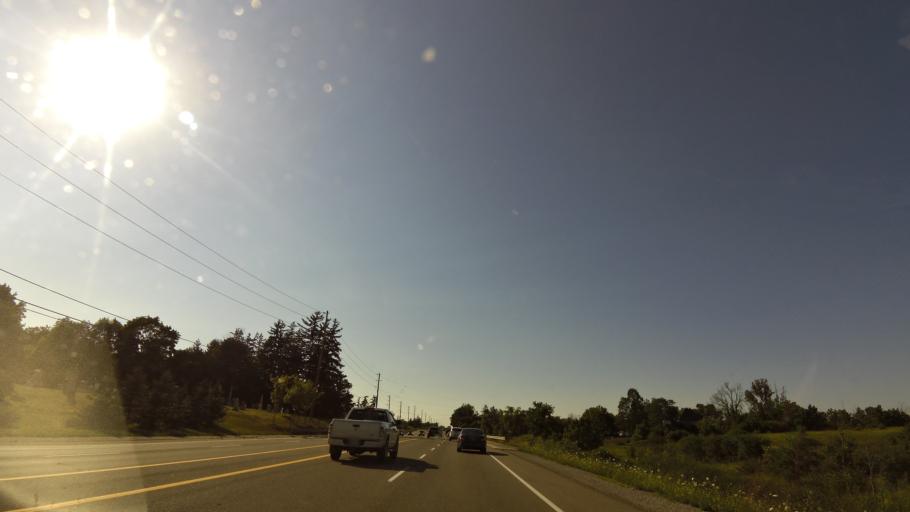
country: CA
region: Ontario
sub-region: Halton
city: Milton
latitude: 43.5391
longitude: -79.7858
